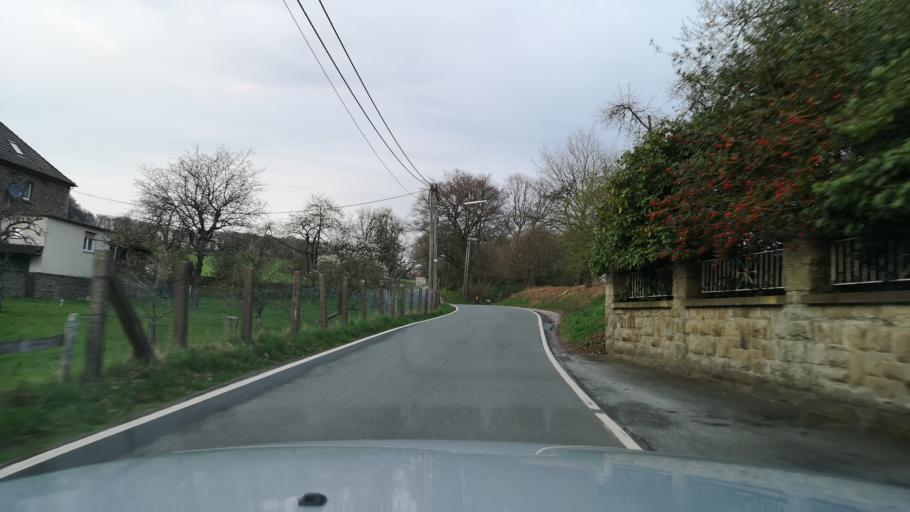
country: DE
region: North Rhine-Westphalia
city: Sprockhovel
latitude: 51.3617
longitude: 7.2334
